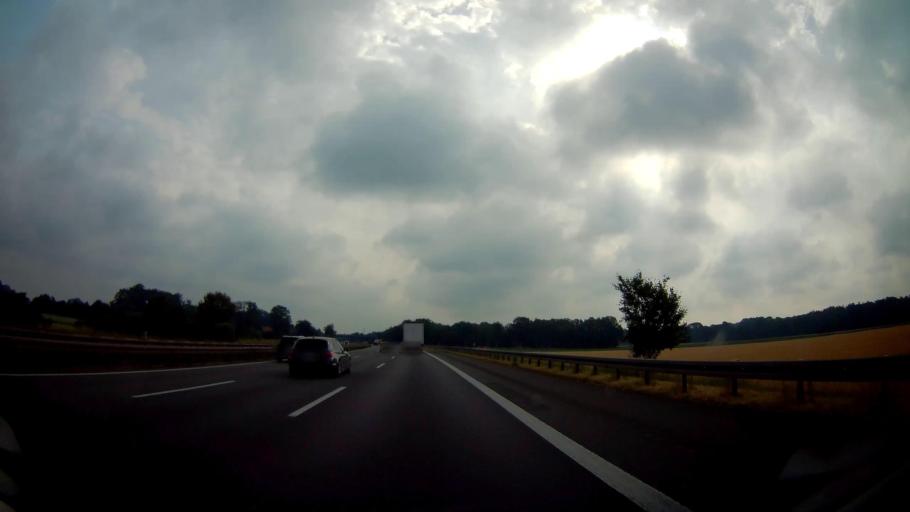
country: DE
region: North Rhine-Westphalia
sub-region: Regierungsbezirk Detmold
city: Guetersloh
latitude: 51.8724
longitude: 8.4134
